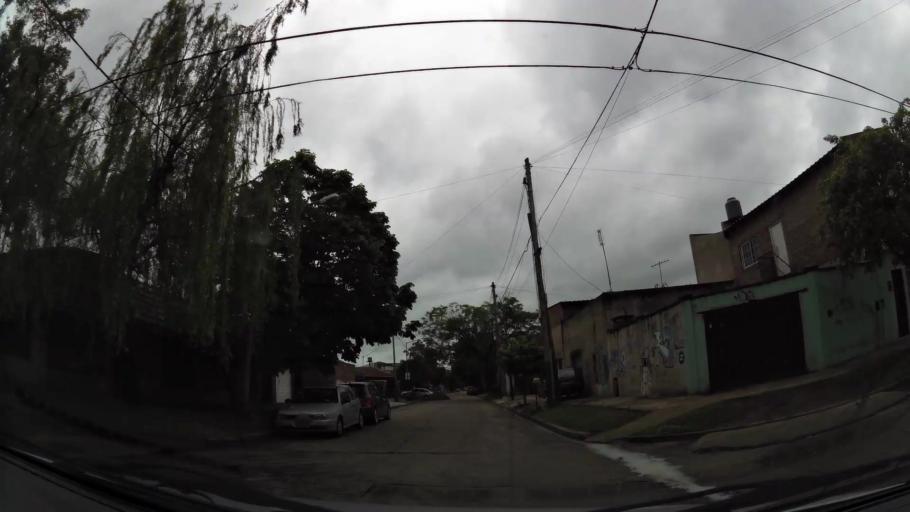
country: AR
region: Buenos Aires
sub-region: Partido de Lomas de Zamora
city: Lomas de Zamora
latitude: -34.7529
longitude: -58.3725
